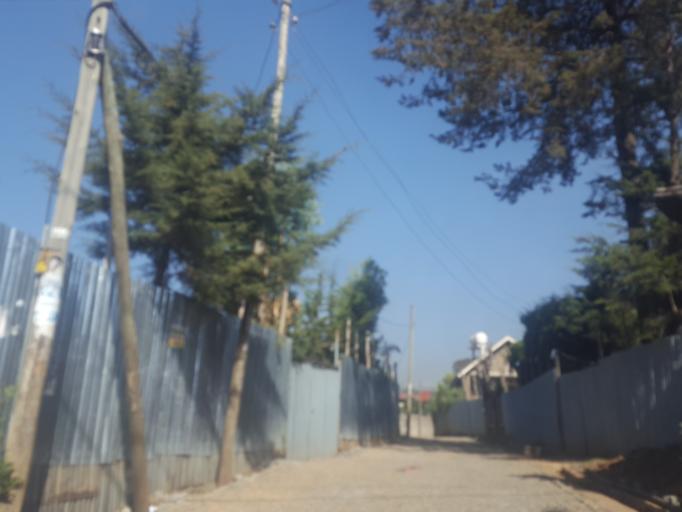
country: ET
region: Adis Abeba
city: Addis Ababa
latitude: 9.0548
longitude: 38.7234
